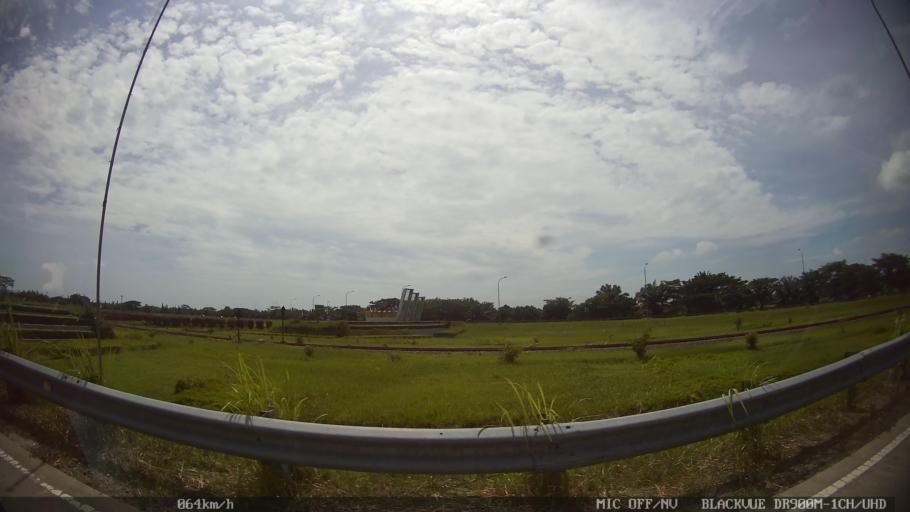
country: ID
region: North Sumatra
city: Percut
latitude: 3.6294
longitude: 98.8726
